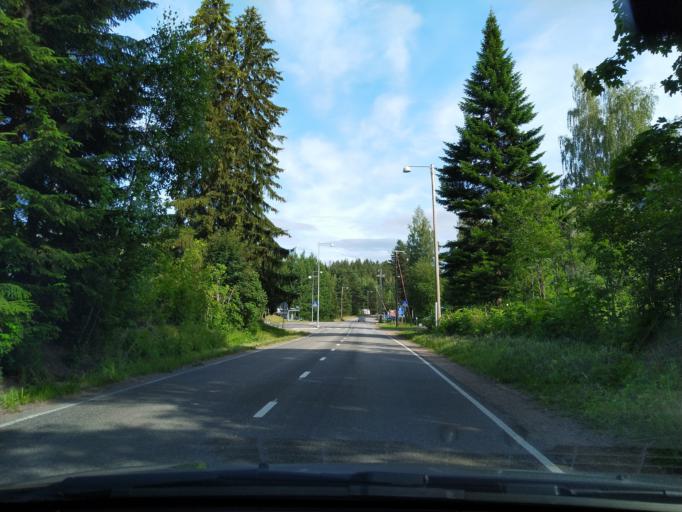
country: FI
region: Kymenlaakso
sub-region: Kouvola
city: Kouvola
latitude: 61.0907
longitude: 26.7932
